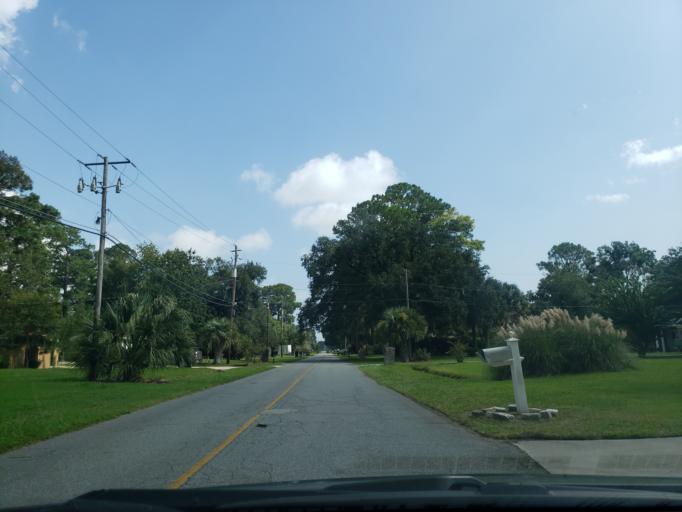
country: US
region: Georgia
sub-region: Chatham County
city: Montgomery
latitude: 31.9323
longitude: -81.0912
